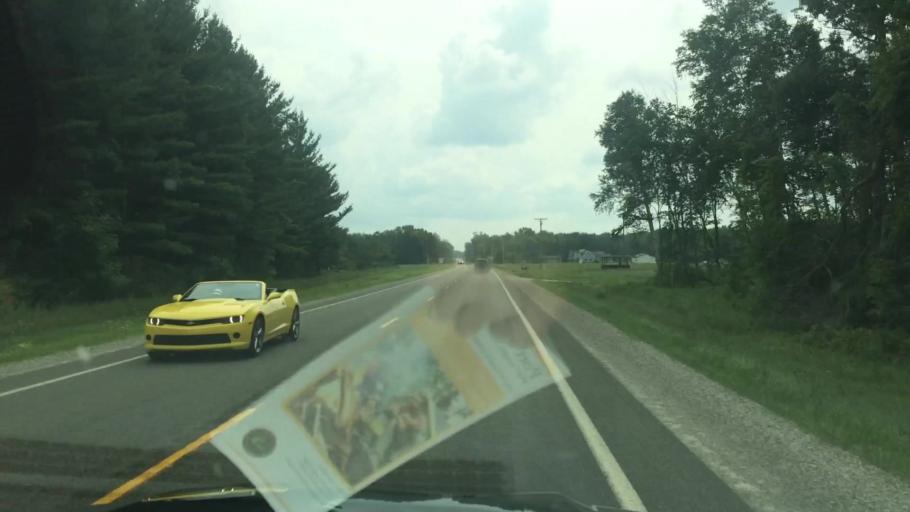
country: US
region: Michigan
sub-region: Tuscola County
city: Cass City
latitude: 43.6498
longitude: -83.0983
